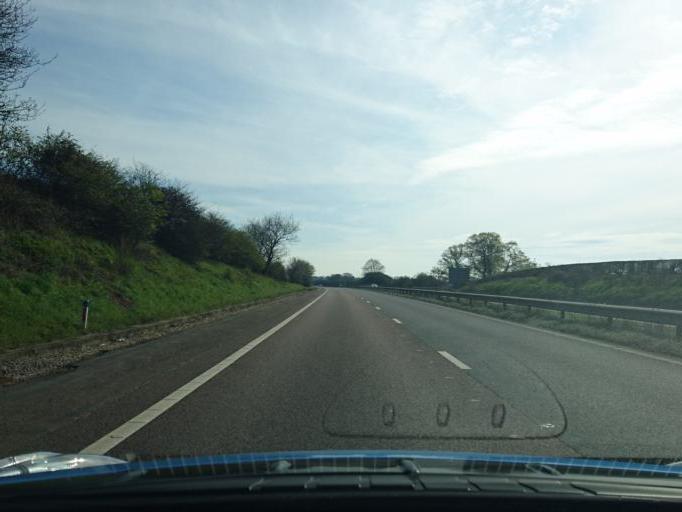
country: GB
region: England
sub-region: Herefordshire
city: Donnington
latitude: 51.9949
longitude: -2.3453
